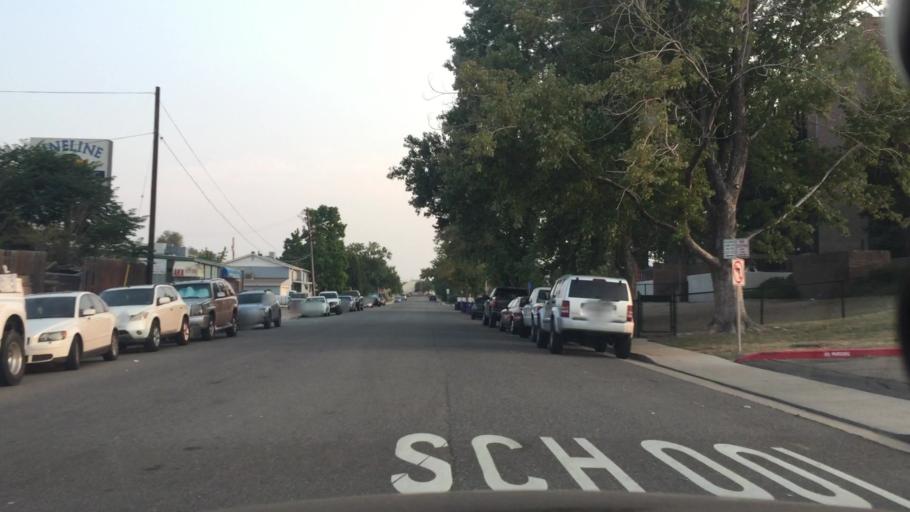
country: US
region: Colorado
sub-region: Arapahoe County
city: Sheridan
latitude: 39.6785
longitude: -105.0181
